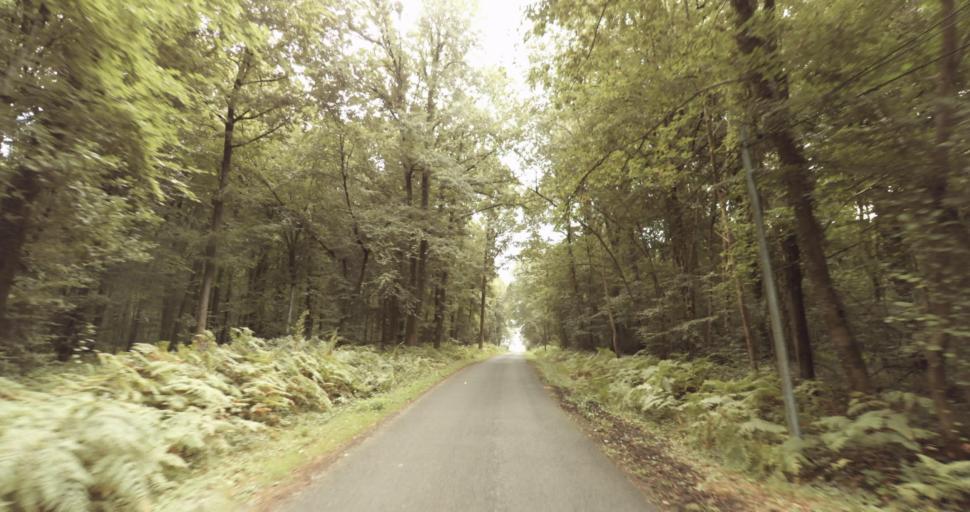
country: FR
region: Lower Normandy
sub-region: Departement de l'Orne
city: Gace
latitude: 48.8282
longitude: 0.2591
